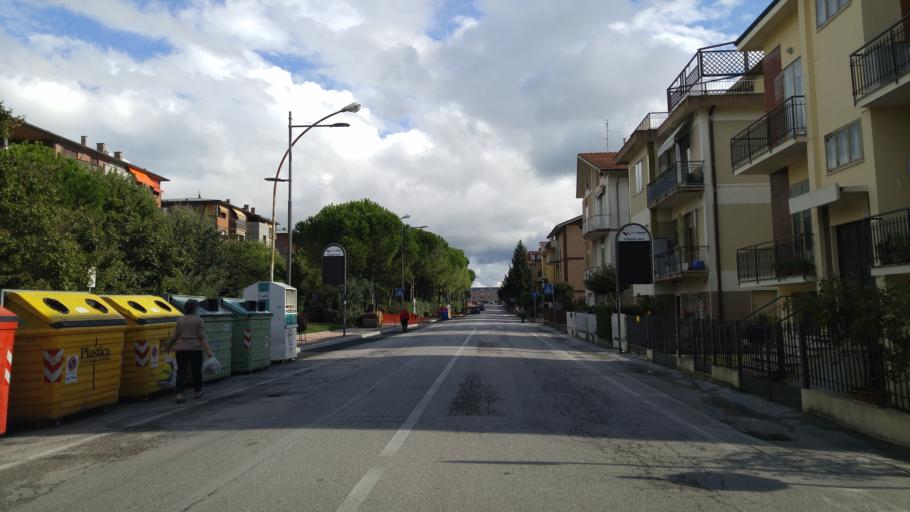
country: IT
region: The Marches
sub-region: Provincia di Pesaro e Urbino
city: Pesaro
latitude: 43.9030
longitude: 12.8973
